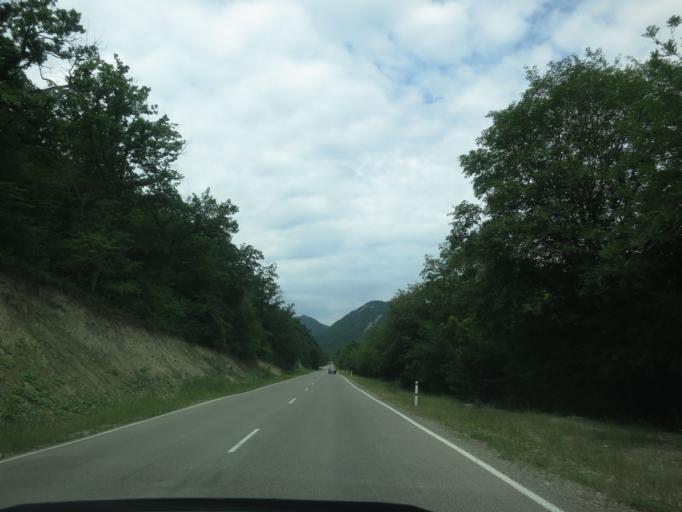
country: GE
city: Didi Lilo
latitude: 41.8064
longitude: 45.1455
